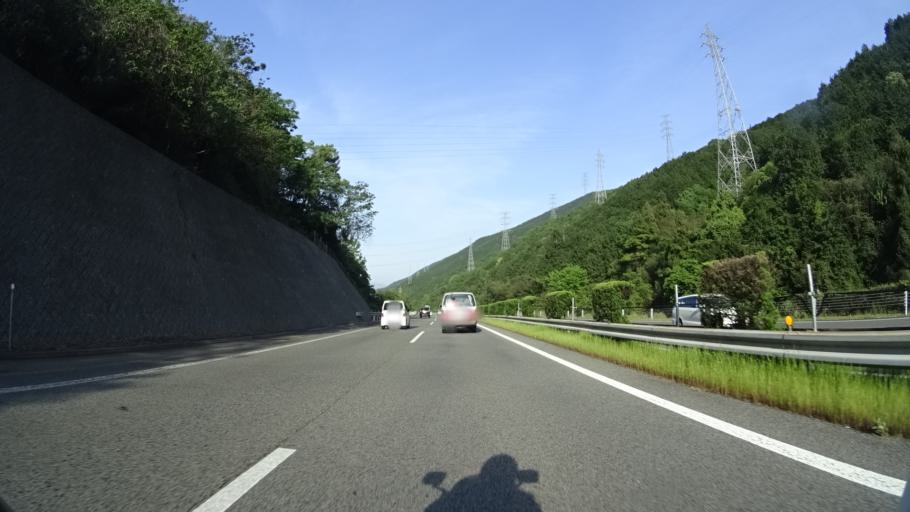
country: JP
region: Ehime
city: Niihama
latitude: 33.9417
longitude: 133.3950
